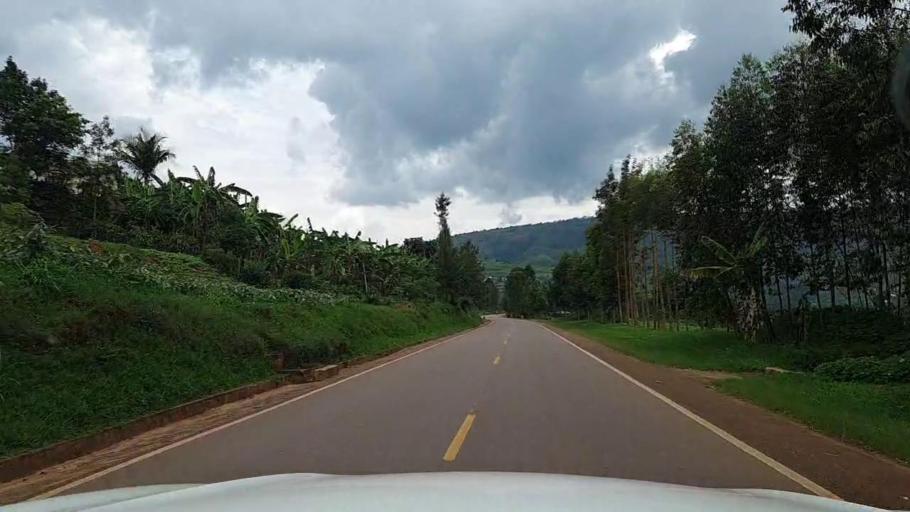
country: RW
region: Kigali
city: Kigali
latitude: -1.7859
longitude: 30.1291
